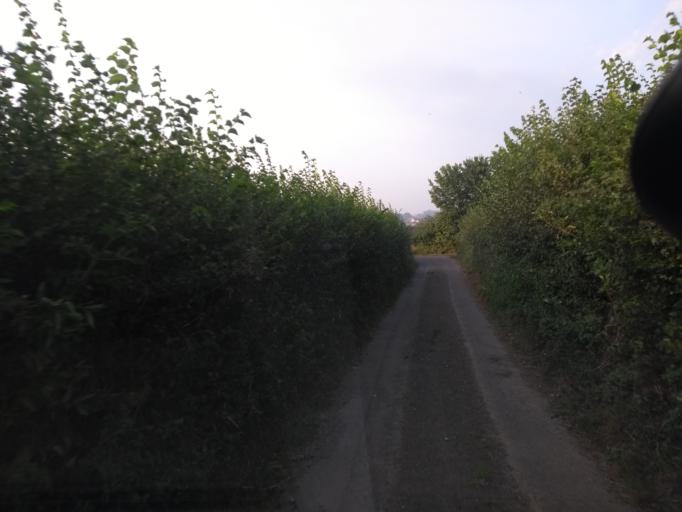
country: GB
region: England
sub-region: Somerset
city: Creech Saint Michael
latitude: 50.9930
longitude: -2.9649
